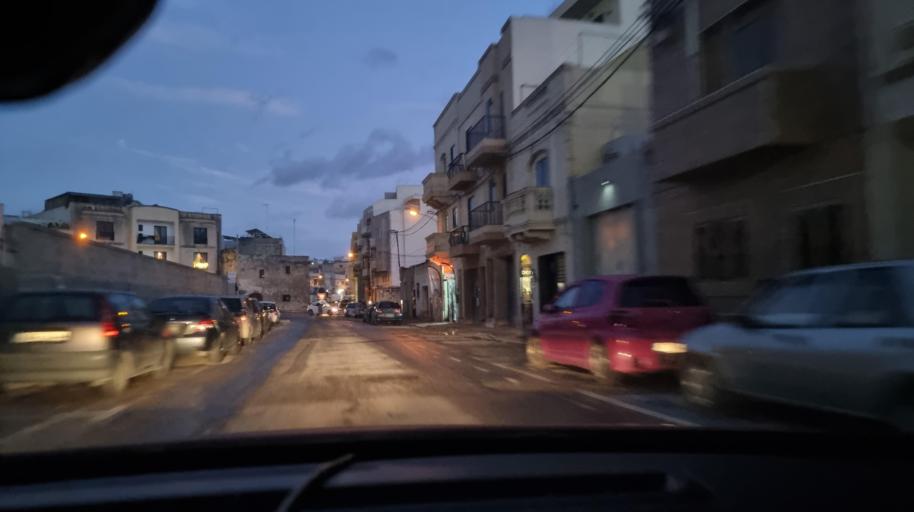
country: MT
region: Il-Hamrun
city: Hamrun
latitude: 35.8821
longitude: 14.4773
